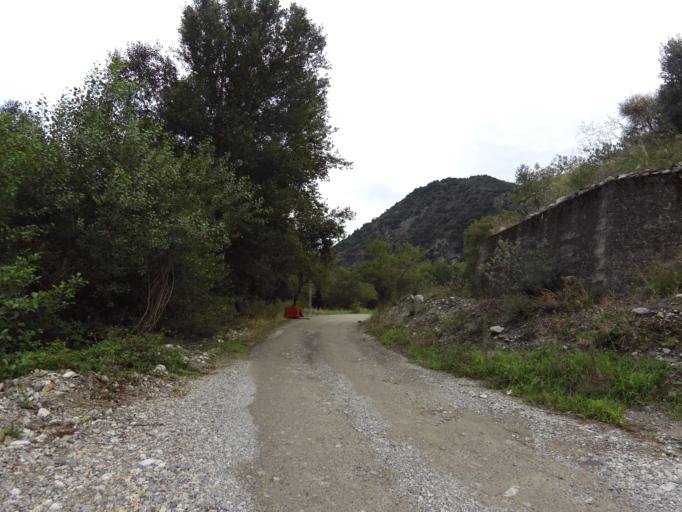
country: IT
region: Calabria
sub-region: Provincia di Reggio Calabria
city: Caulonia
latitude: 38.4243
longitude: 16.3780
